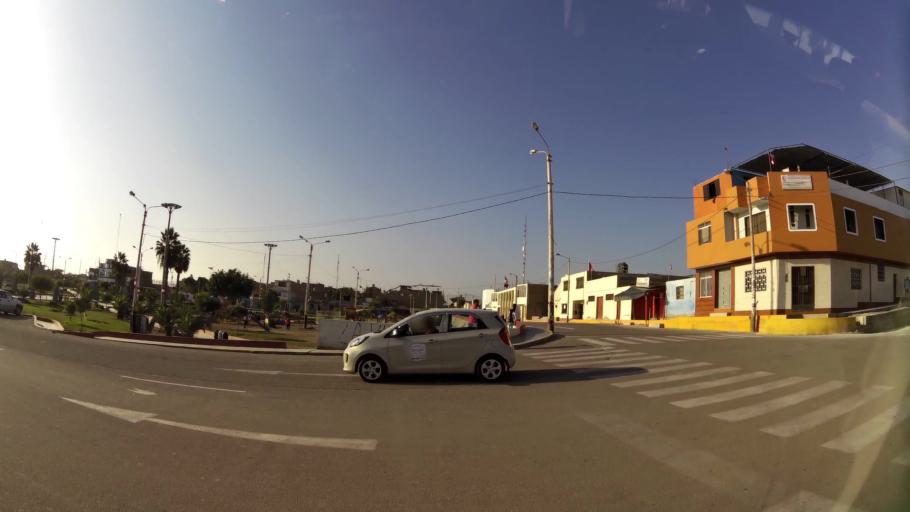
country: PE
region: Ica
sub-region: Provincia de Pisco
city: Villa Tupac Amaru
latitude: -13.7141
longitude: -76.1486
